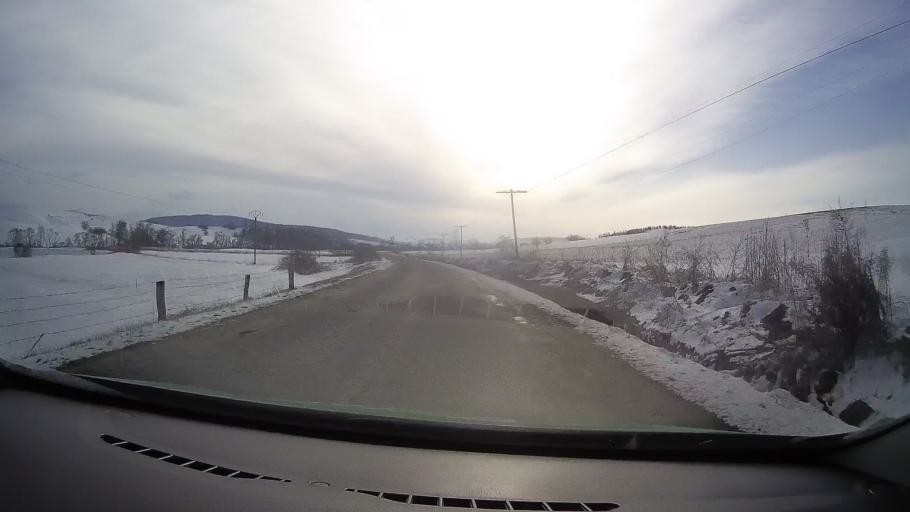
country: RO
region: Sibiu
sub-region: Oras Agnita
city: Ruja
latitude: 46.0094
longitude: 24.6831
